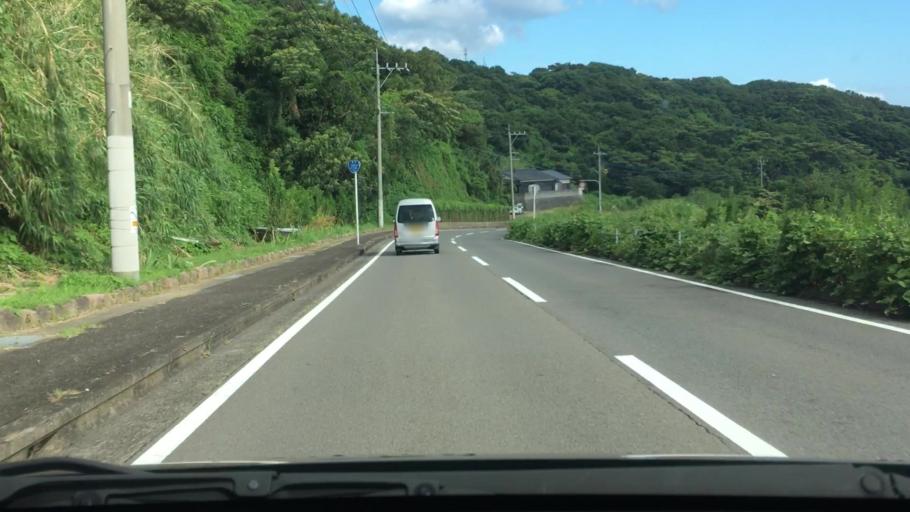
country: JP
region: Nagasaki
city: Togitsu
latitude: 32.8482
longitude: 129.6933
